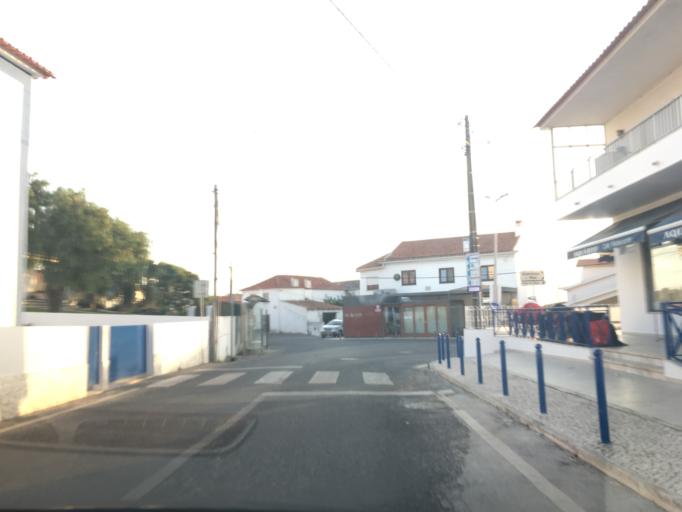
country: PT
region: Lisbon
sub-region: Sintra
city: Colares
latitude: 38.8264
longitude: -9.4373
